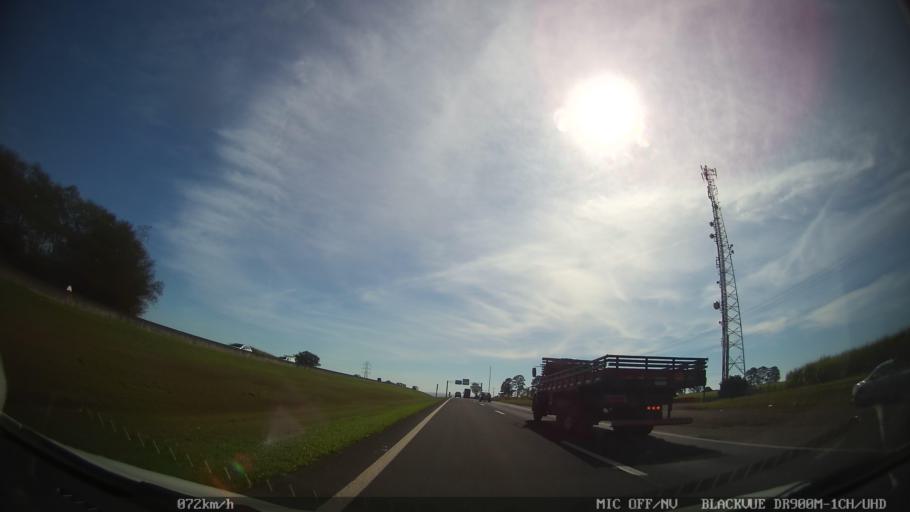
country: BR
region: Sao Paulo
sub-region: Leme
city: Leme
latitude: -22.2635
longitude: -47.3907
